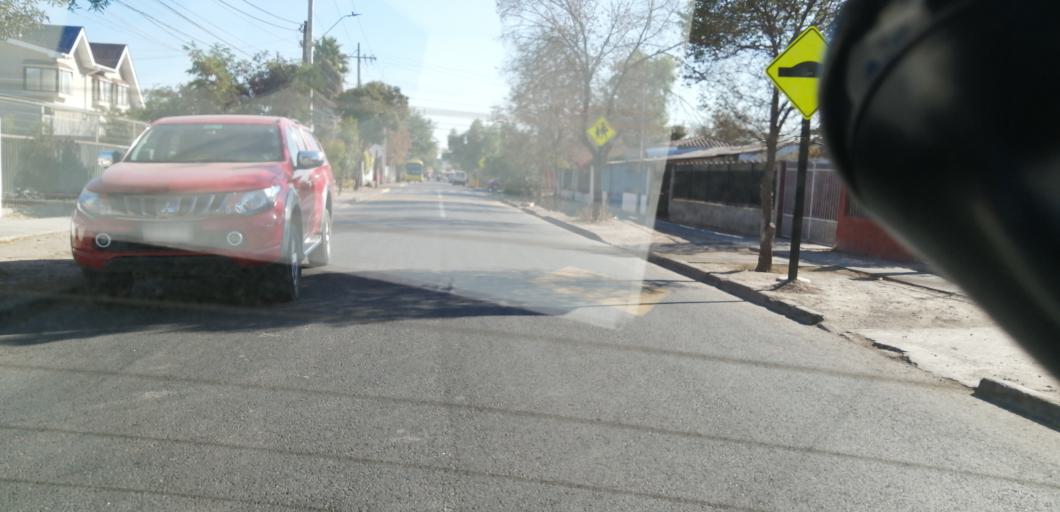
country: CL
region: Santiago Metropolitan
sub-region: Provincia de Santiago
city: Lo Prado
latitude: -33.4388
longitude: -70.7615
